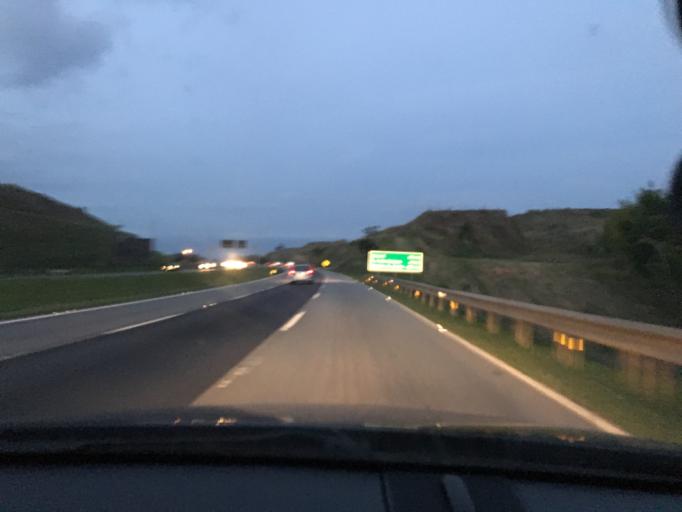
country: BR
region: Sao Paulo
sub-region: Santa Isabel
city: Santa Isabel
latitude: -23.3822
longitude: -46.1496
